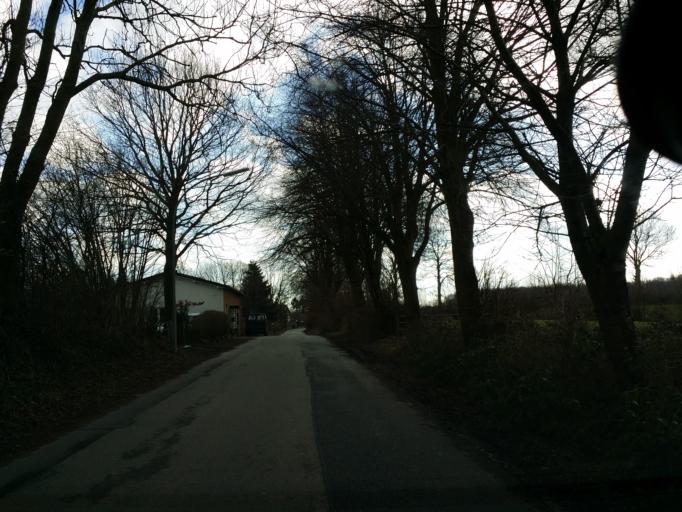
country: DE
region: Schleswig-Holstein
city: Krummwisch
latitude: 54.3090
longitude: 9.9060
